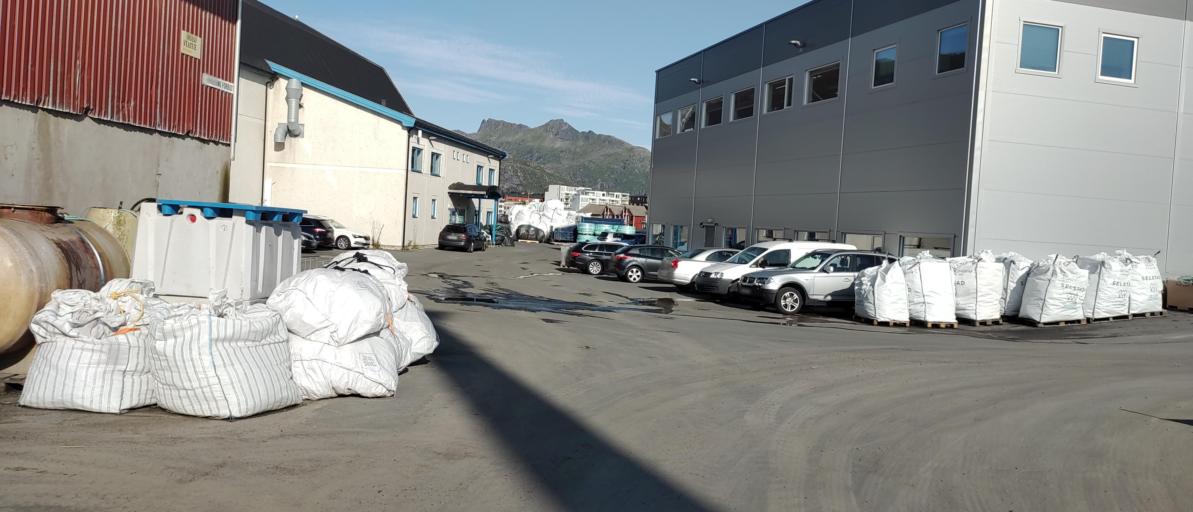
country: NO
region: Nordland
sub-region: Vagan
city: Svolvaer
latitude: 68.2299
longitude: 14.5740
